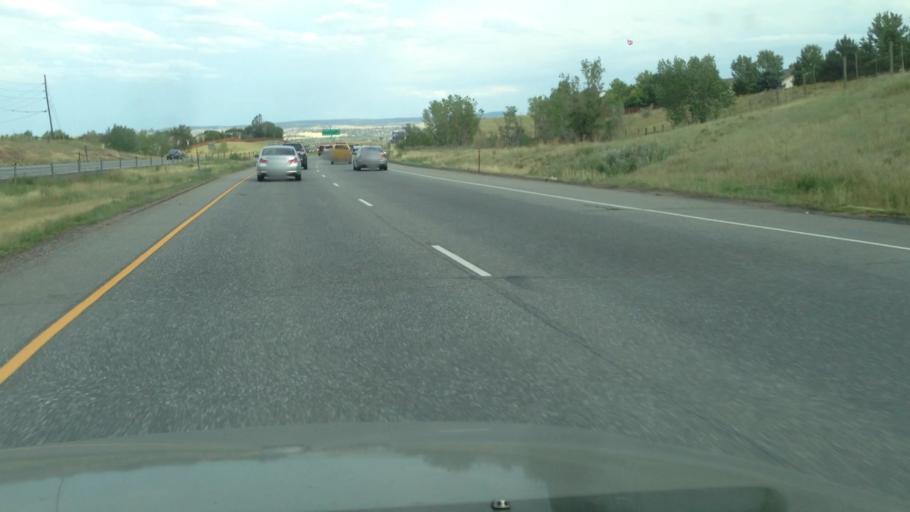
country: US
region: Colorado
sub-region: Jefferson County
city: Ken Caryl
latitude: 39.5585
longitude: -105.1015
